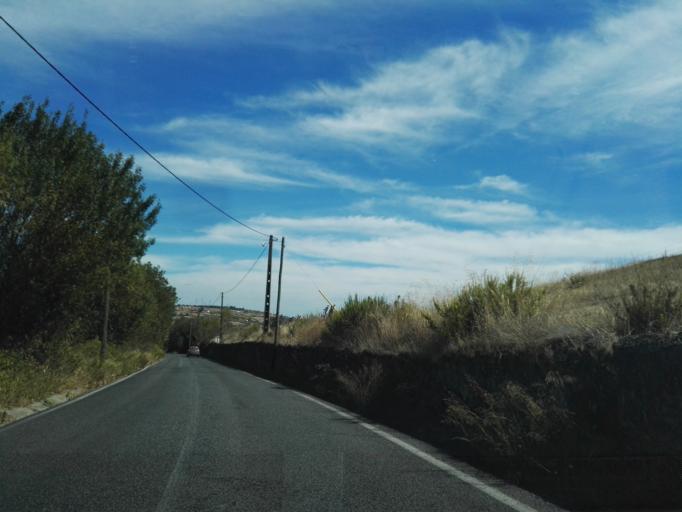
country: PT
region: Lisbon
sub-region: Vila Franca de Xira
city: Sao Joao dos Montes
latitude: 38.9475
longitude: -9.0530
